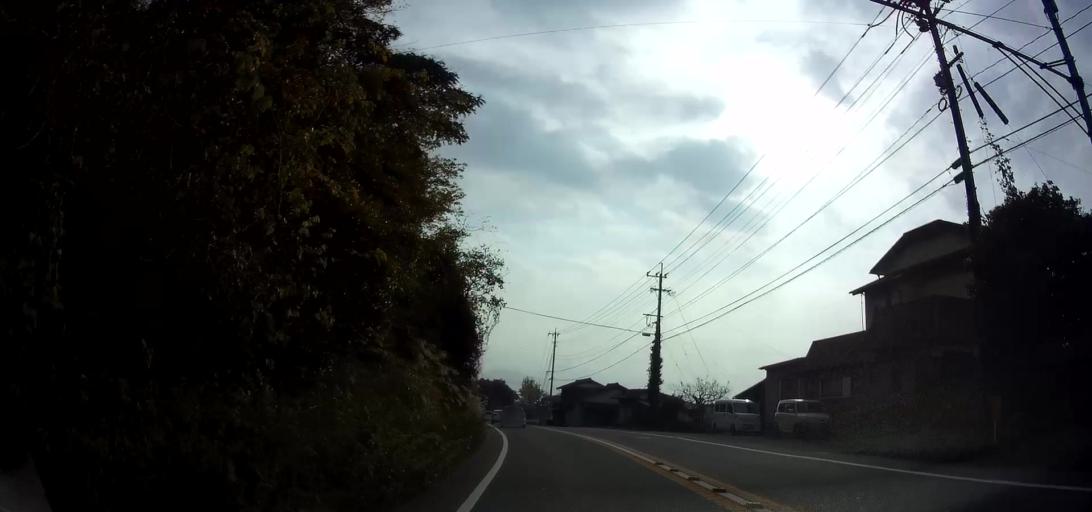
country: JP
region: Nagasaki
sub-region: Isahaya-shi
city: Isahaya
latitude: 32.7969
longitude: 130.1347
